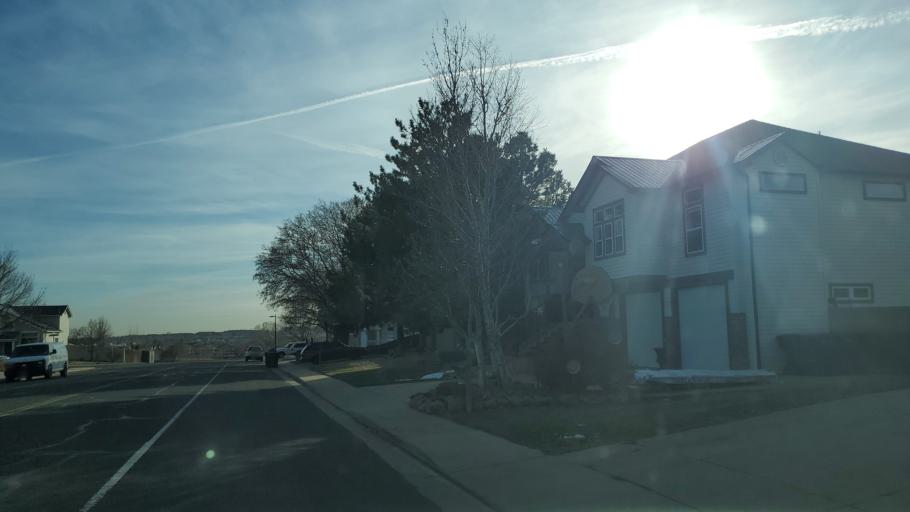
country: US
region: Colorado
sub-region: Adams County
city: Northglenn
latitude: 39.9033
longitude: -104.9539
